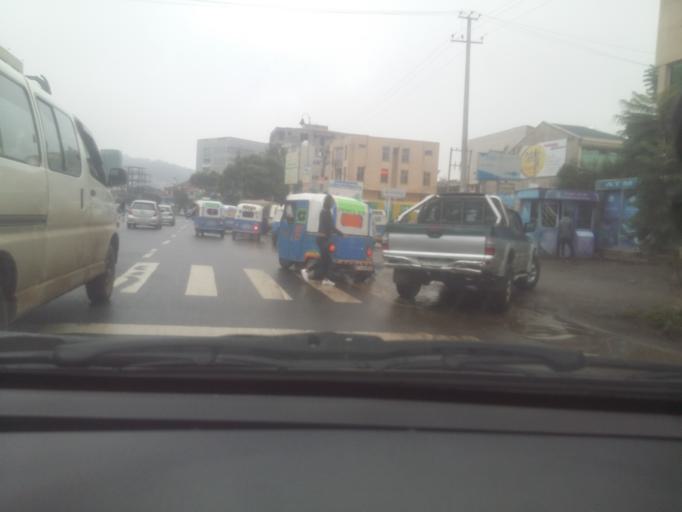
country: ET
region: Adis Abeba
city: Addis Ababa
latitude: 8.9502
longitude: 38.7191
